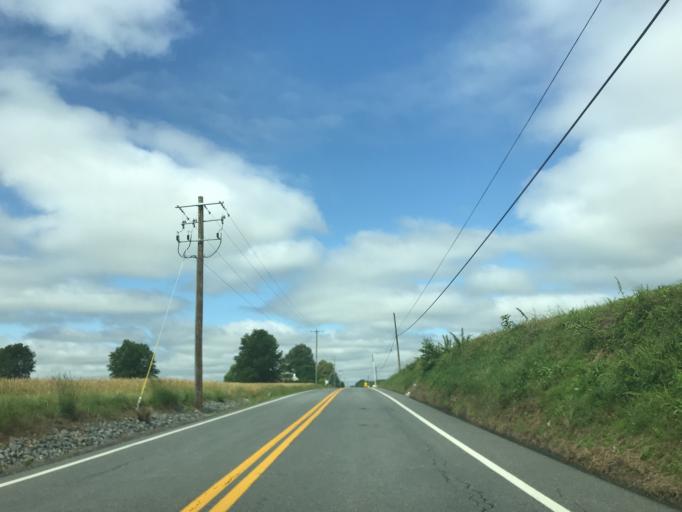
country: US
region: Maryland
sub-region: Caroline County
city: Ridgely
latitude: 38.8854
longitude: -75.9697
